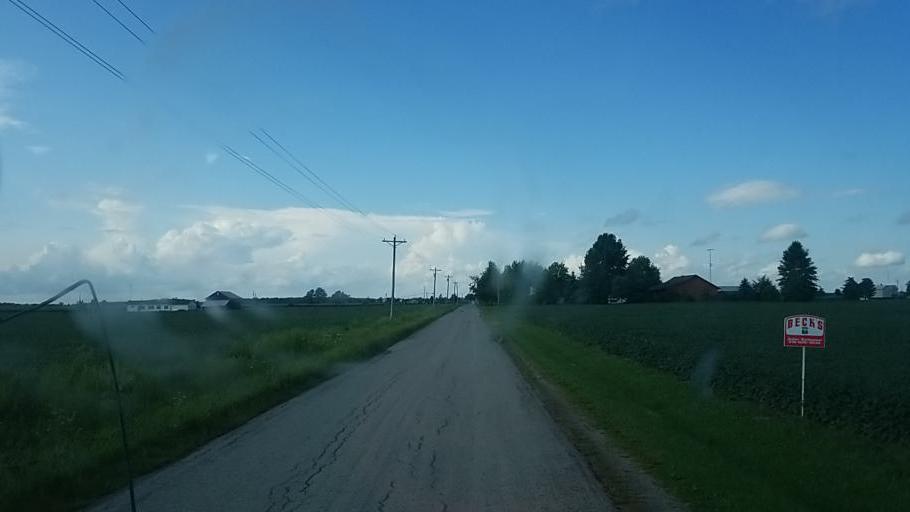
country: US
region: Ohio
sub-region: Hardin County
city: Forest
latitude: 40.7995
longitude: -83.3997
